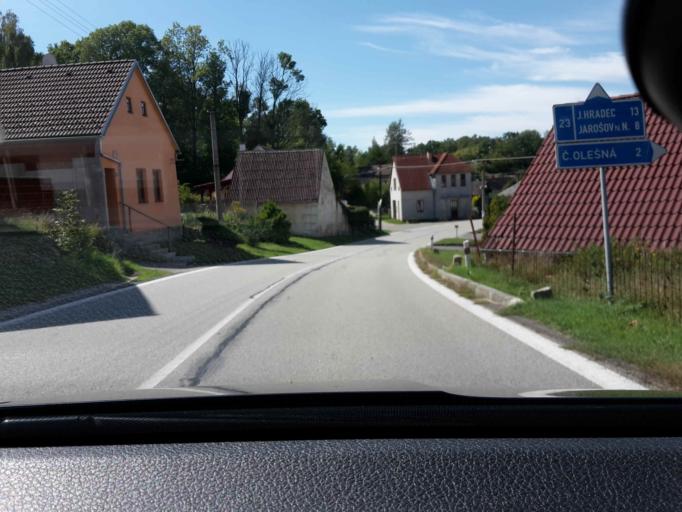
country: CZ
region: Jihocesky
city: Strmilov
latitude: 49.1754
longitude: 15.1606
